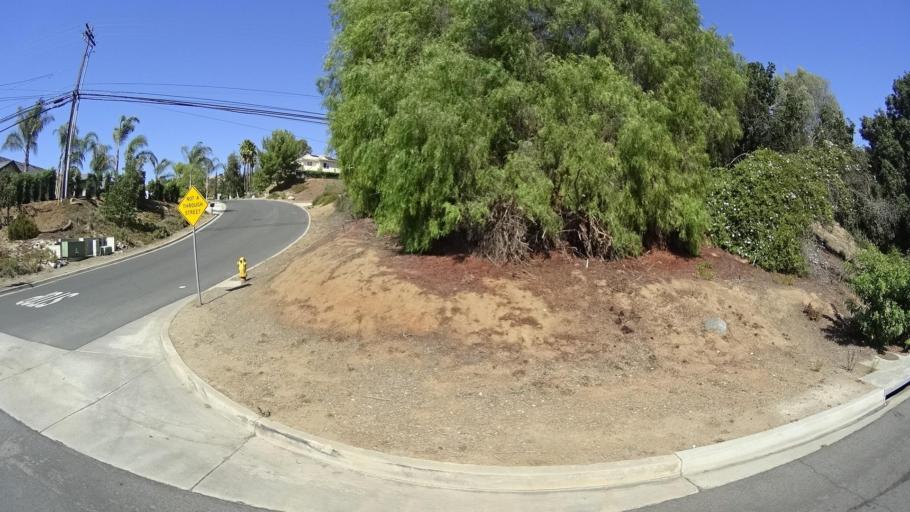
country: US
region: California
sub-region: San Diego County
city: Granite Hills
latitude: 32.8032
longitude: -116.9003
